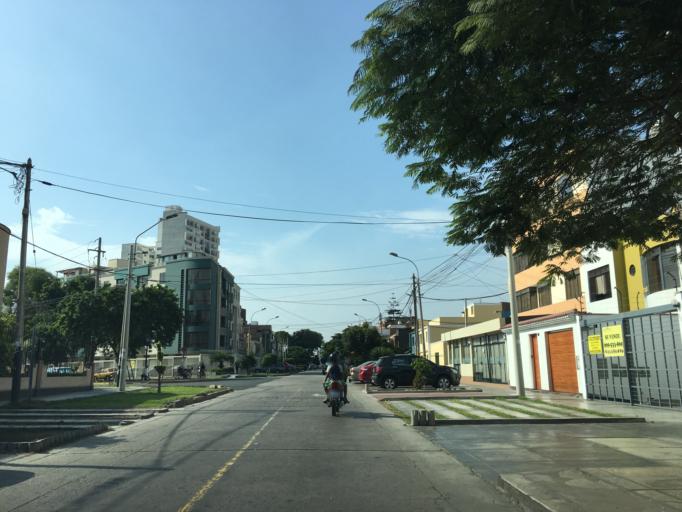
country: PE
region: Lima
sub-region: Lima
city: San Isidro
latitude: -12.0747
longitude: -77.0620
